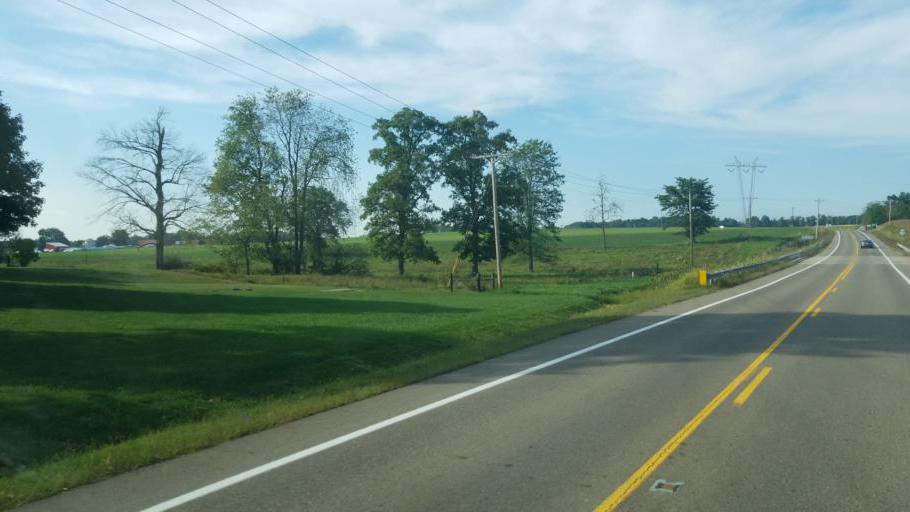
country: US
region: Ohio
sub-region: Knox County
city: Oak Hill
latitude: 40.3427
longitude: -82.3014
